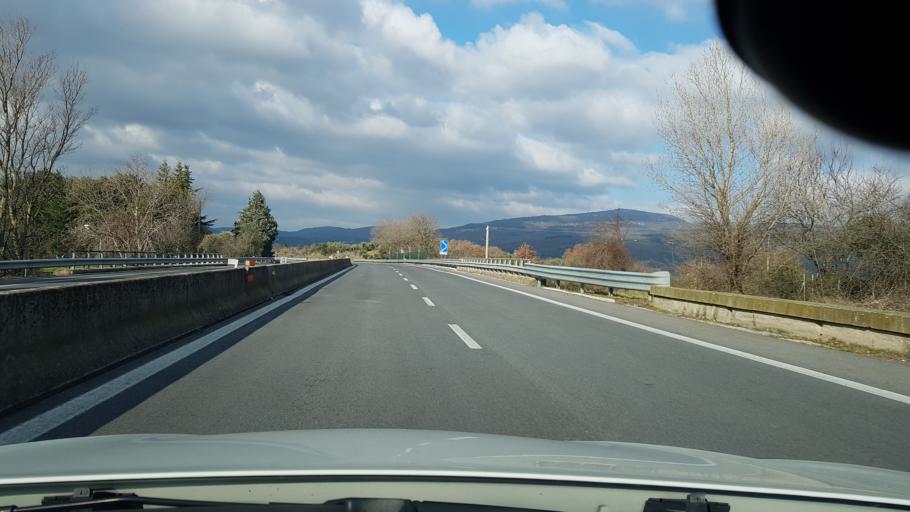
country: IT
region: Umbria
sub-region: Provincia di Perugia
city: Passignano sul Trasimeno
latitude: 43.1963
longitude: 12.1321
